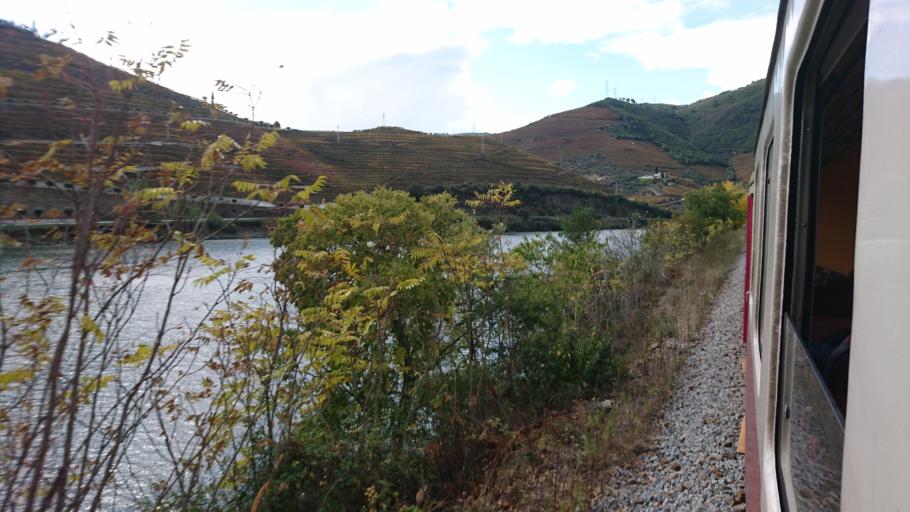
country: PT
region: Viseu
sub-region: Armamar
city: Armamar
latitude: 41.1442
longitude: -7.6940
